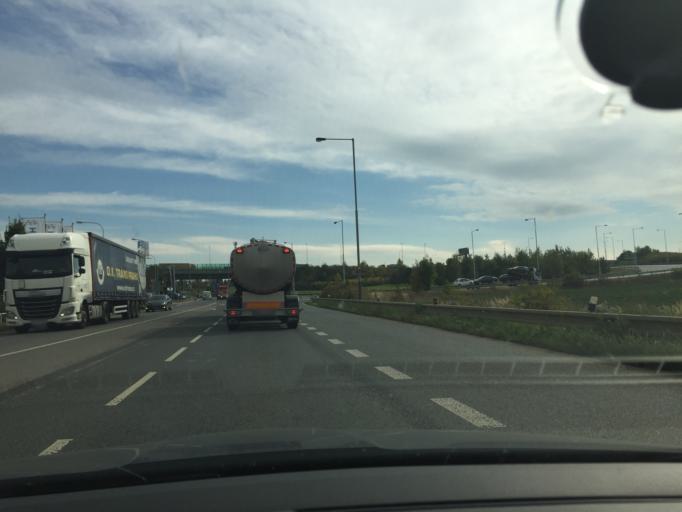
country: CZ
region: Praha
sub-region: Praha 14
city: Dolni Pocernice
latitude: 50.0820
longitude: 14.5891
